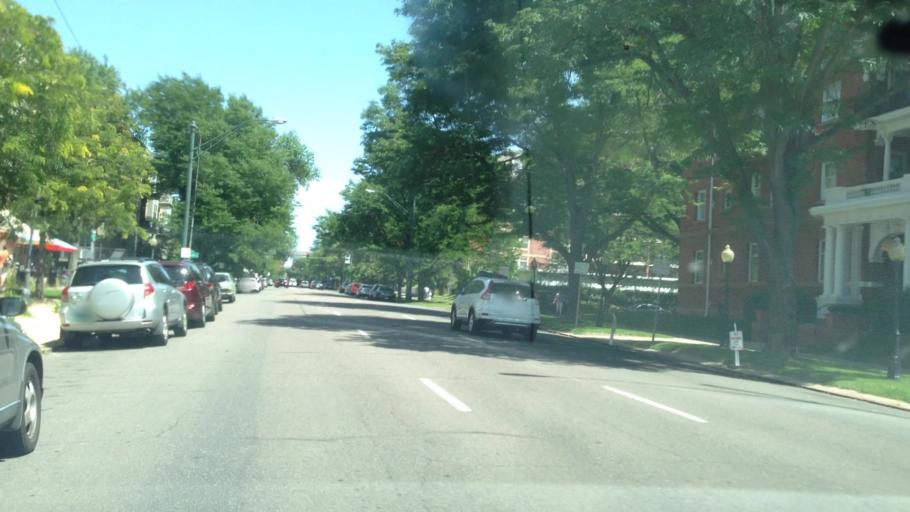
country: US
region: Colorado
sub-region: Denver County
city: Denver
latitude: 39.7433
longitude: -104.9770
